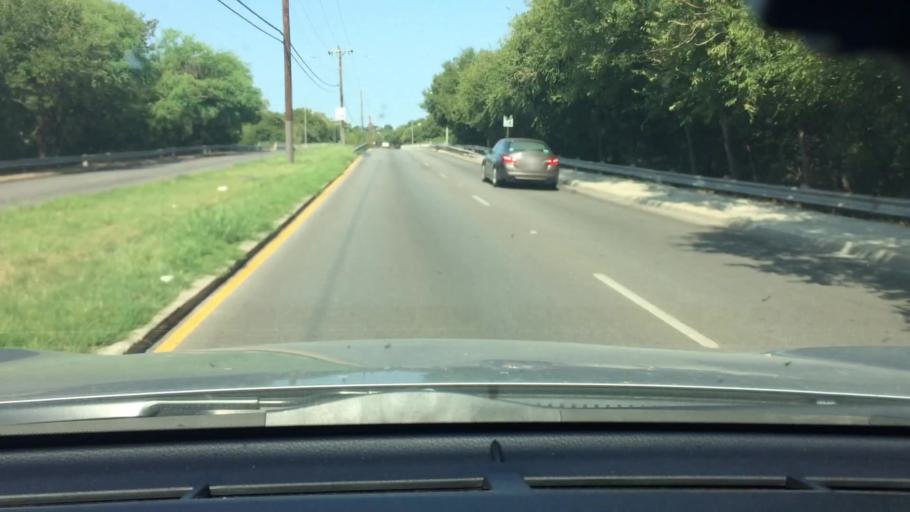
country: US
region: Texas
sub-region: Bexar County
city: China Grove
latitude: 29.3748
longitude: -98.4235
